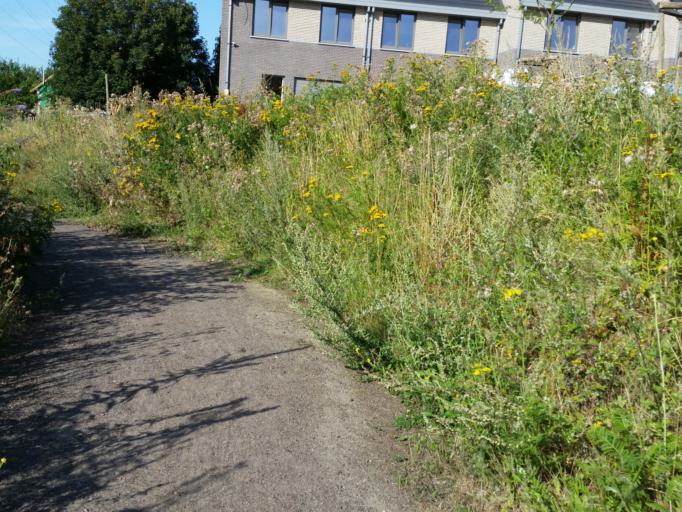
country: BE
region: Flanders
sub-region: Provincie Vlaams-Brabant
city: Diegem
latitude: 50.8842
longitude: 4.4055
